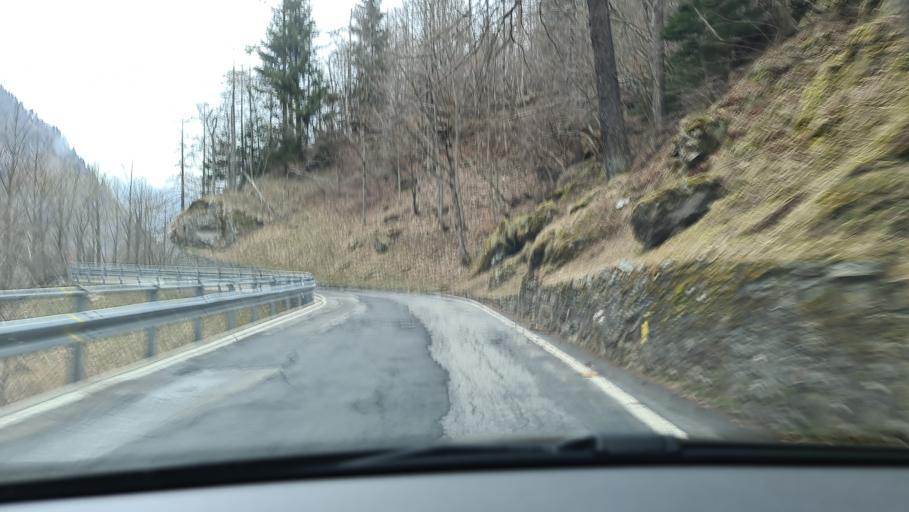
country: CH
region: Ticino
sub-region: Vallemaggia District
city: Cevio
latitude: 46.4186
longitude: 8.6519
